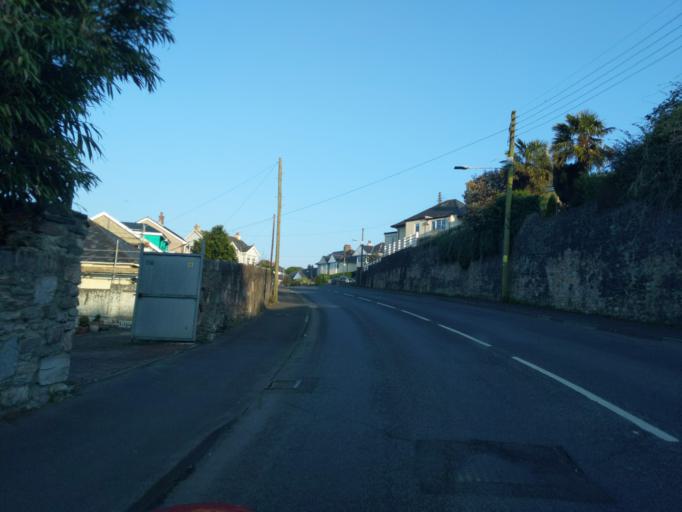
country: GB
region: England
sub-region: Plymouth
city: Plymstock
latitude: 50.3563
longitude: -4.0879
